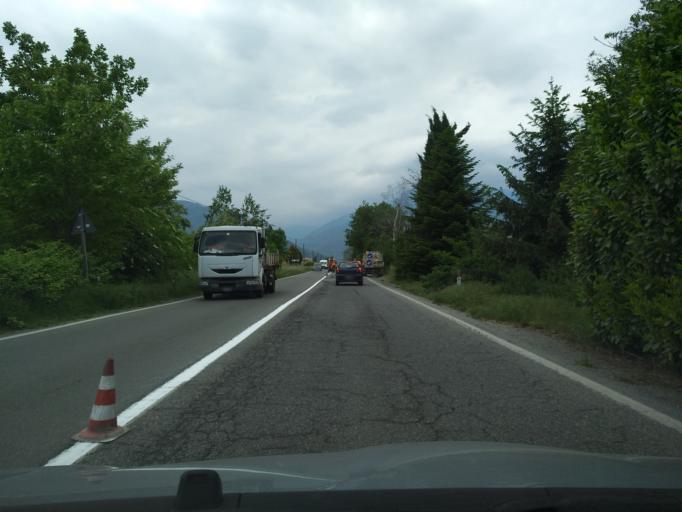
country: IT
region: Piedmont
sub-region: Provincia di Torino
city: Bibiana
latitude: 44.8104
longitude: 7.2803
